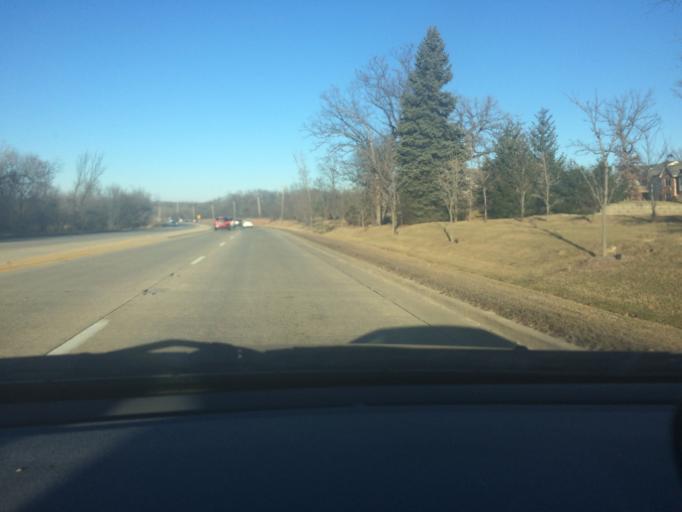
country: US
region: Illinois
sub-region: Cook County
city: Streamwood
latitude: 42.0398
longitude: -88.1958
